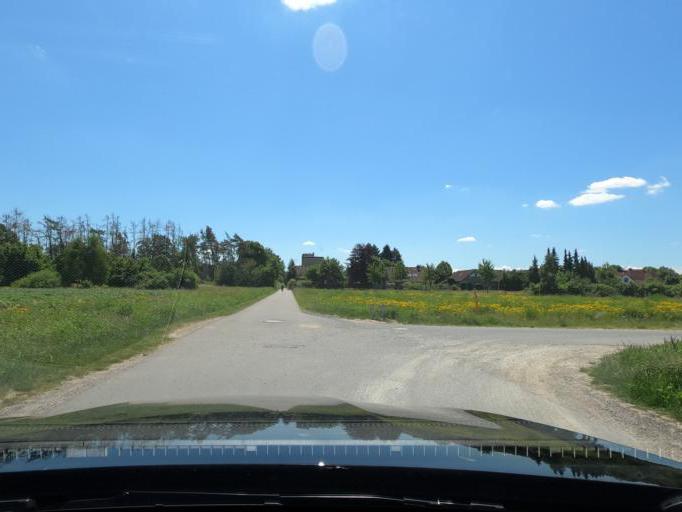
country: DE
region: Lower Saxony
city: Burgdorf
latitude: 52.4596
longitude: 10.0001
